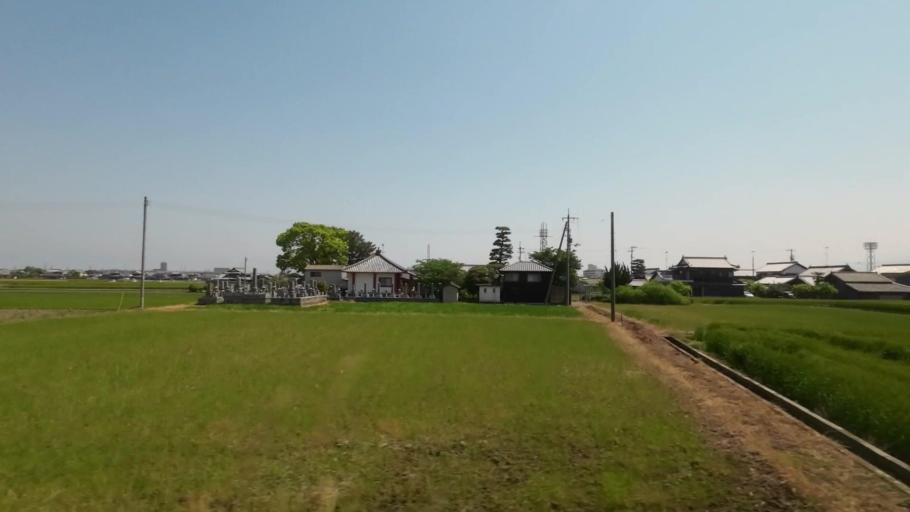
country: JP
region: Ehime
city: Saijo
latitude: 33.9201
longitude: 133.0941
